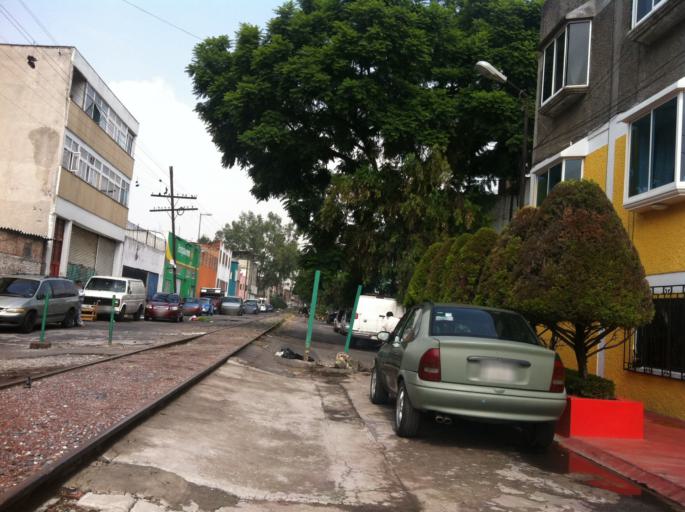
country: MX
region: Mexico City
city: Azcapotzalco
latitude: 19.4598
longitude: -99.1840
